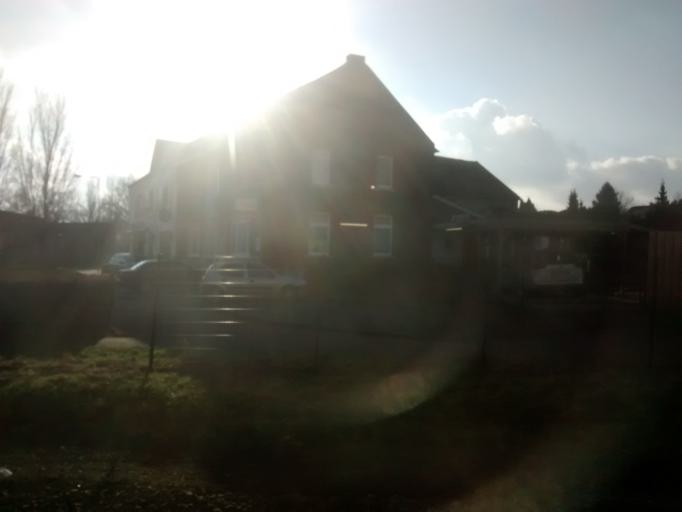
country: NL
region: Limburg
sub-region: Gemeente Schinnen
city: Puth
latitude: 50.9391
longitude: 5.8743
